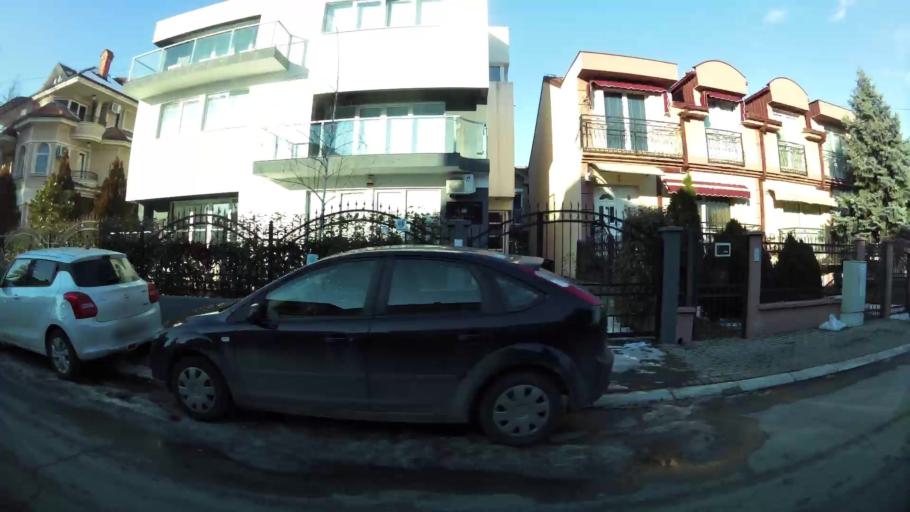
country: MK
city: Krushopek
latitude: 42.0029
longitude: 21.3875
